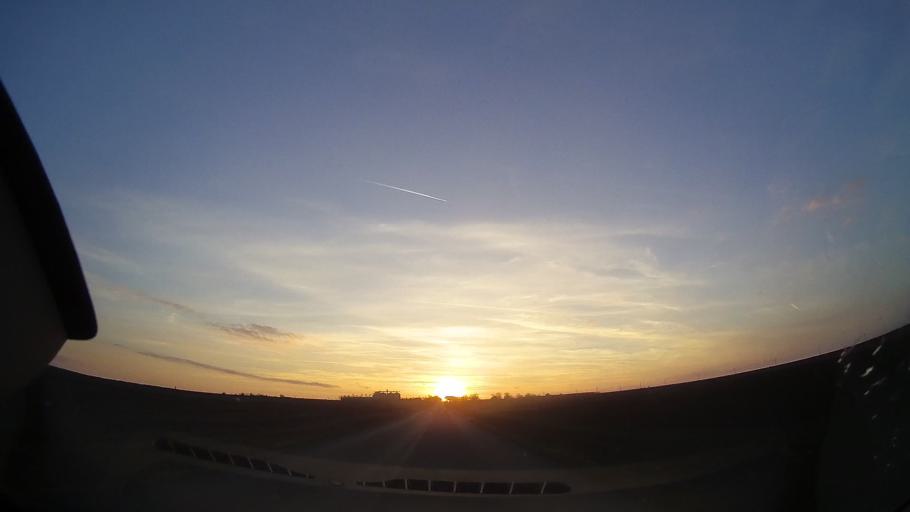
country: RO
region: Constanta
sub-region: Comuna Mereni
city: Mereni
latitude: 44.0238
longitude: 28.3590
